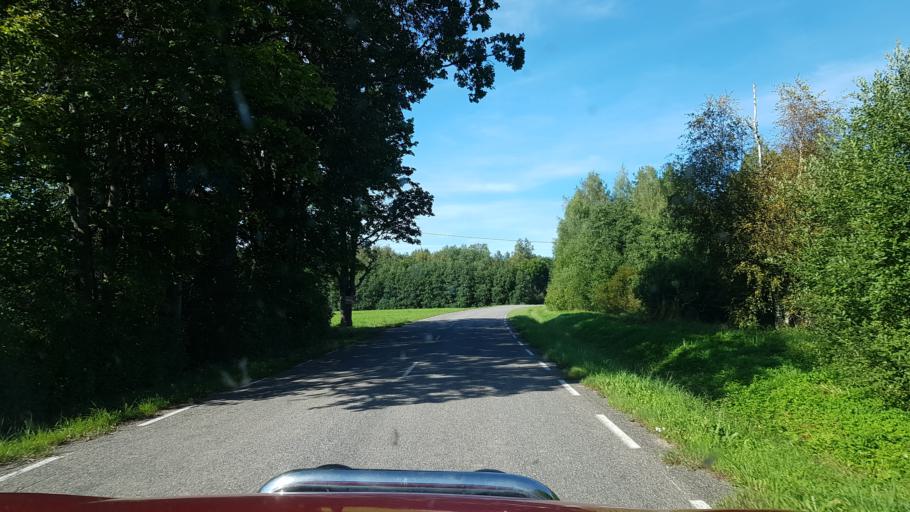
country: EE
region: Paernumaa
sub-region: Saarde vald
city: Kilingi-Nomme
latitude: 58.0301
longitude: 25.0101
